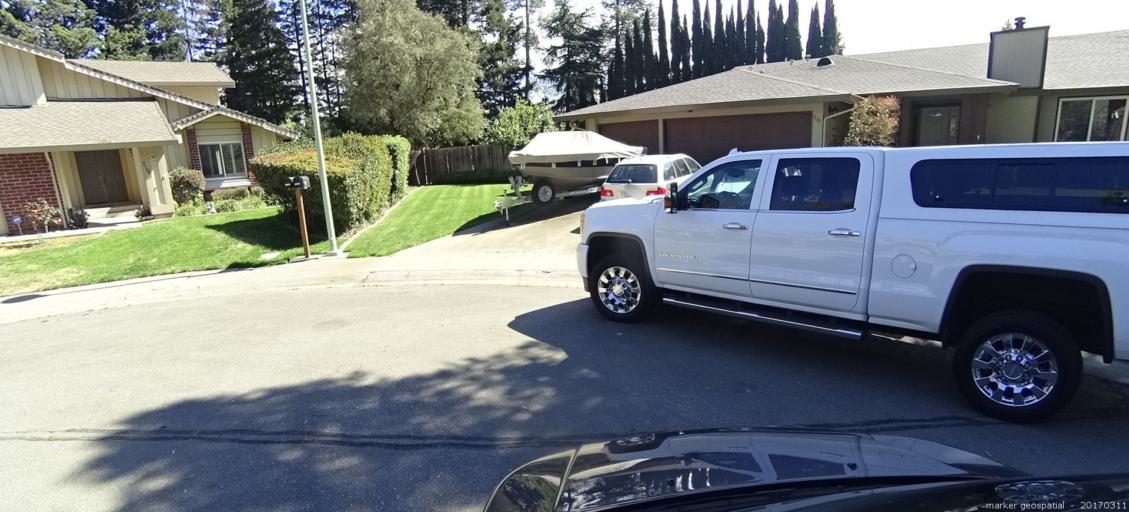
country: US
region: California
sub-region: Yolo County
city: West Sacramento
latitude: 38.4971
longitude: -121.5520
